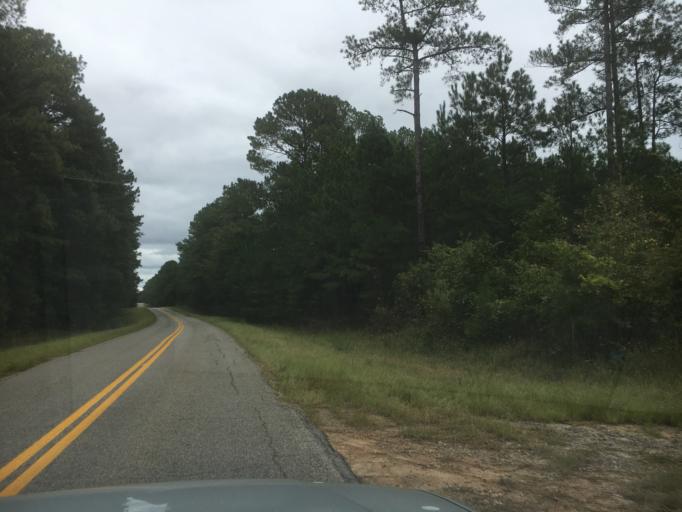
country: US
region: Georgia
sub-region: Wilkes County
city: Washington
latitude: 33.6916
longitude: -82.6006
